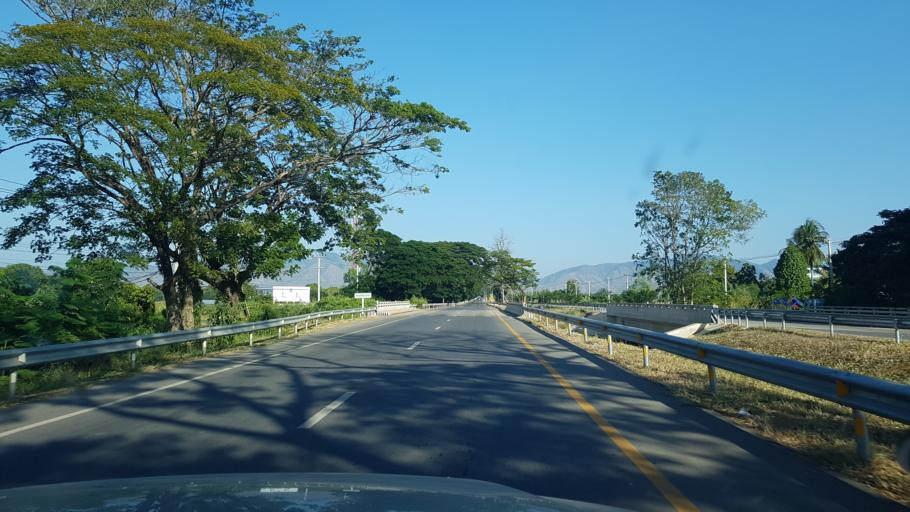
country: TH
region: Phetchabun
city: Lom Sak
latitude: 16.7269
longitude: 101.2540
